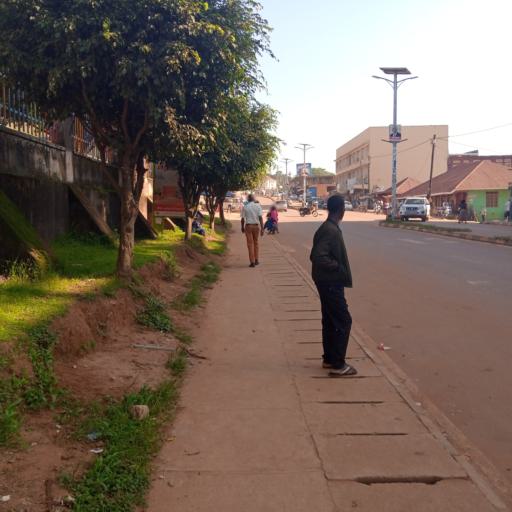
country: UG
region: Central Region
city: Masaka
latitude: -0.3445
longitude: 31.7375
